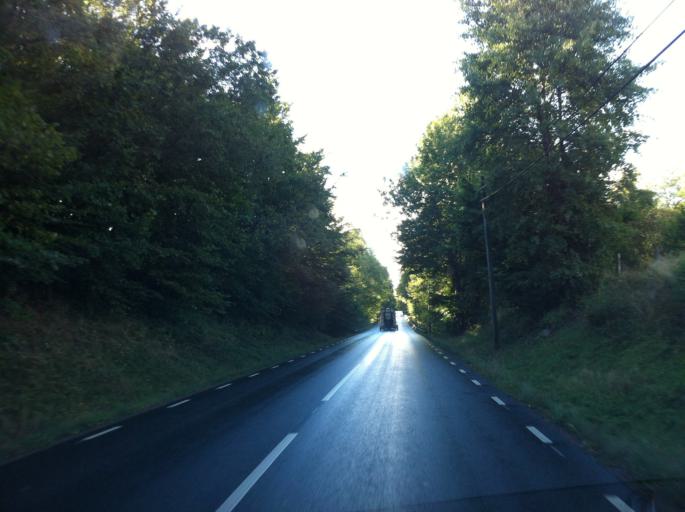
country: SE
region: Skane
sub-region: Hoors Kommun
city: Hoeoer
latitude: 56.0208
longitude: 13.4945
